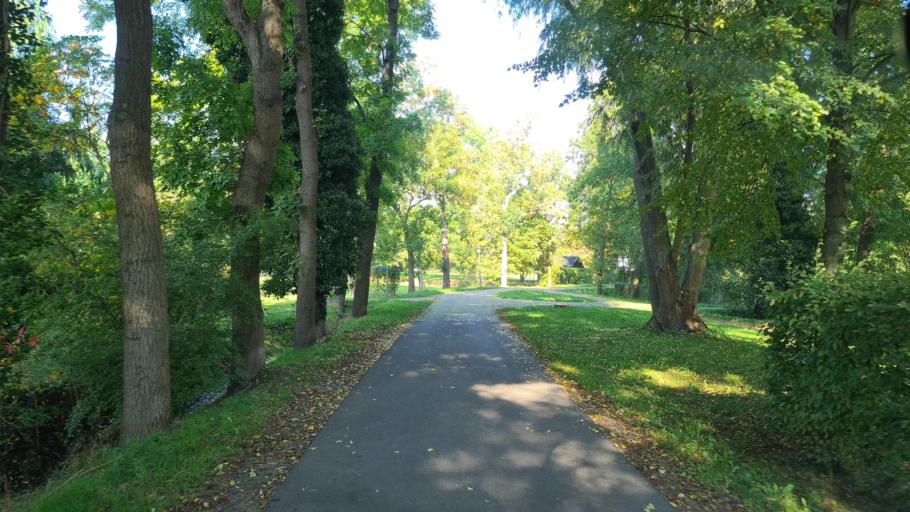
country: DE
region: Brandenburg
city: Luckau
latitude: 51.8484
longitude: 13.7180
